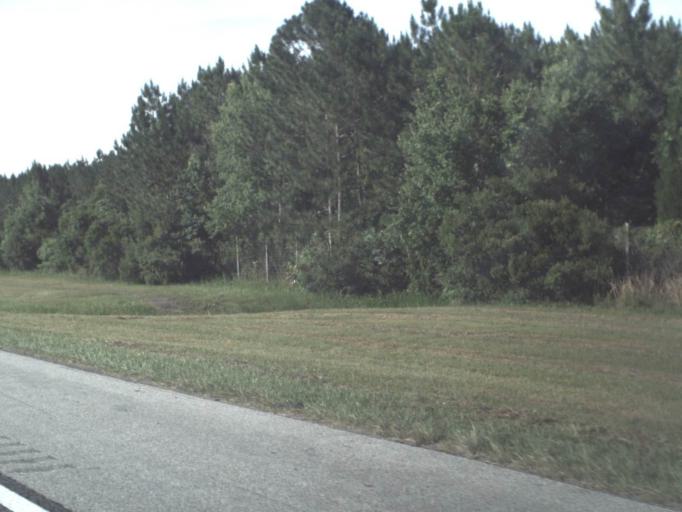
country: US
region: Florida
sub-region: Saint Johns County
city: Saint Augustine Shores
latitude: 29.7558
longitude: -81.3496
